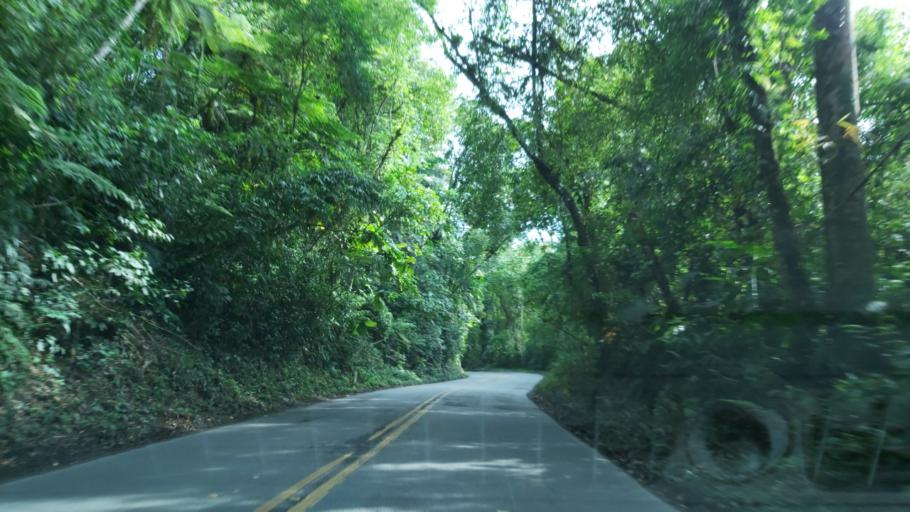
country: BR
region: Sao Paulo
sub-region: Juquia
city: Juquia
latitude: -24.0881
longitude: -47.6142
